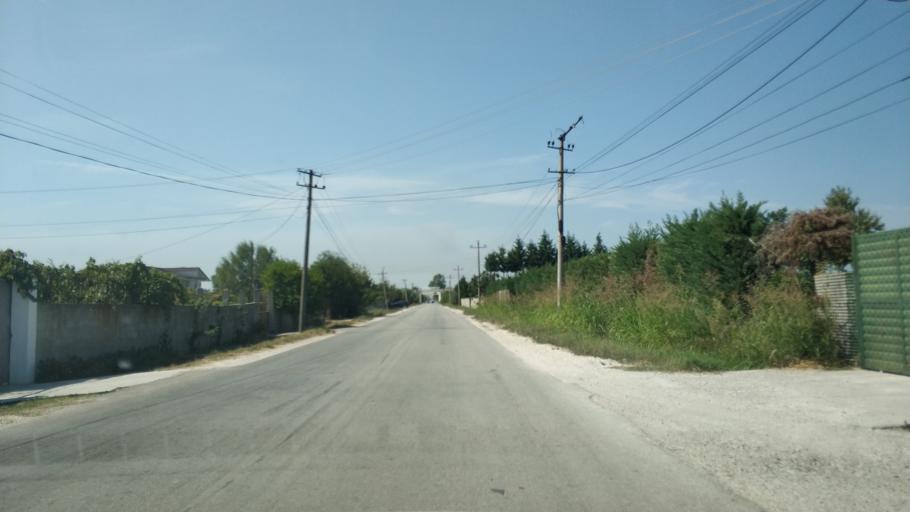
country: AL
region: Fier
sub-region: Rrethi i Fierit
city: Dermenas
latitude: 40.7414
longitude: 19.5059
